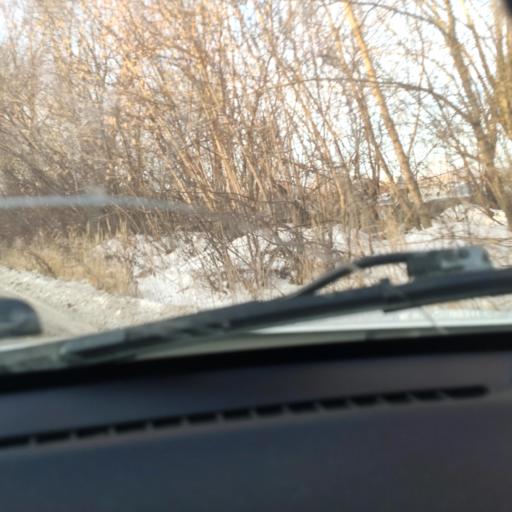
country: RU
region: Tatarstan
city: Verkhniy Uslon
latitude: 55.7984
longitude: 49.0462
